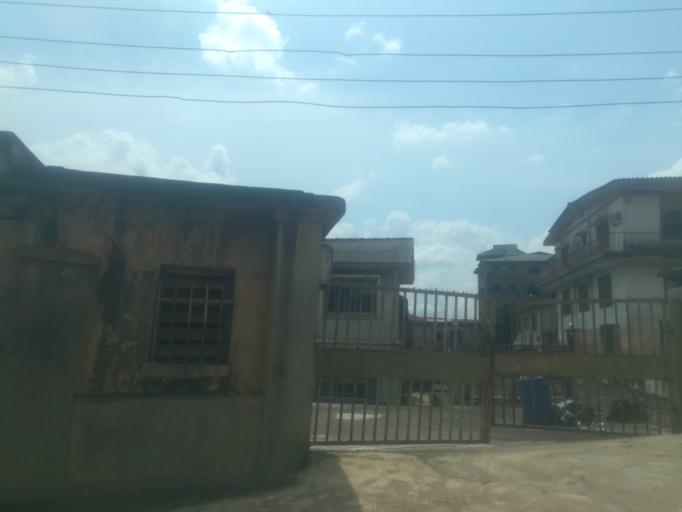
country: NG
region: Oyo
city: Ibadan
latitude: 7.3609
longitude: 3.8805
